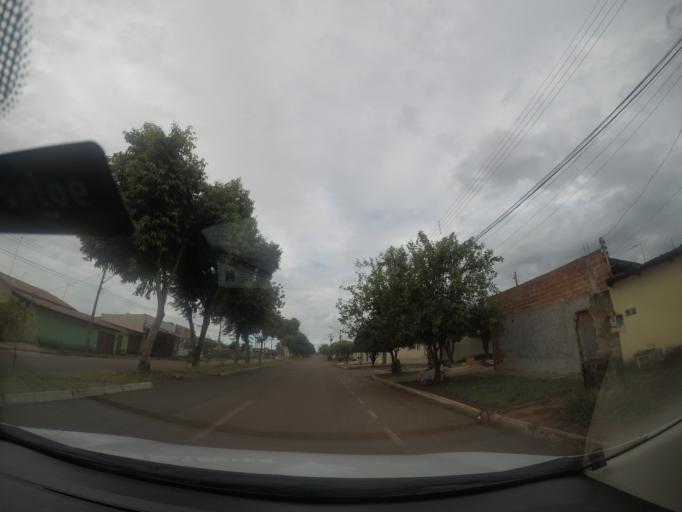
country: BR
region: Goias
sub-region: Goiania
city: Goiania
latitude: -16.5967
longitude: -49.3039
